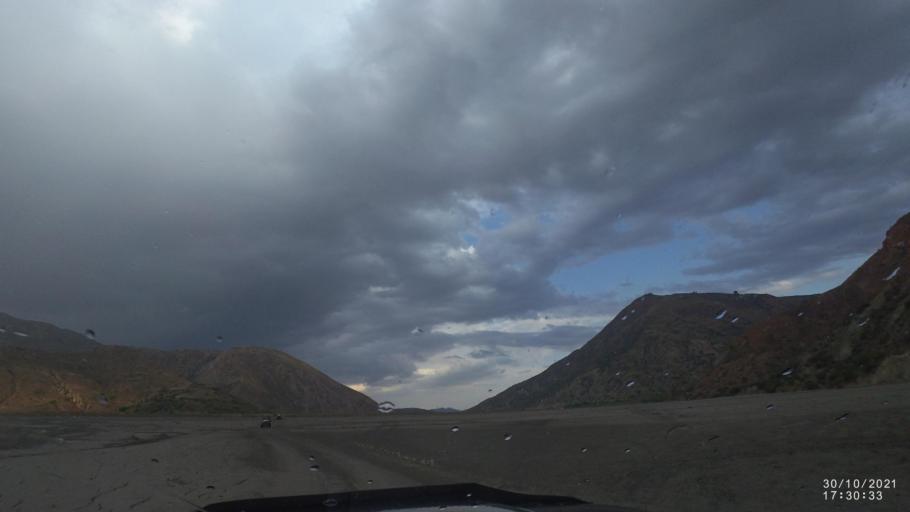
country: BO
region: Cochabamba
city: Sipe Sipe
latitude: -17.5239
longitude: -66.5972
